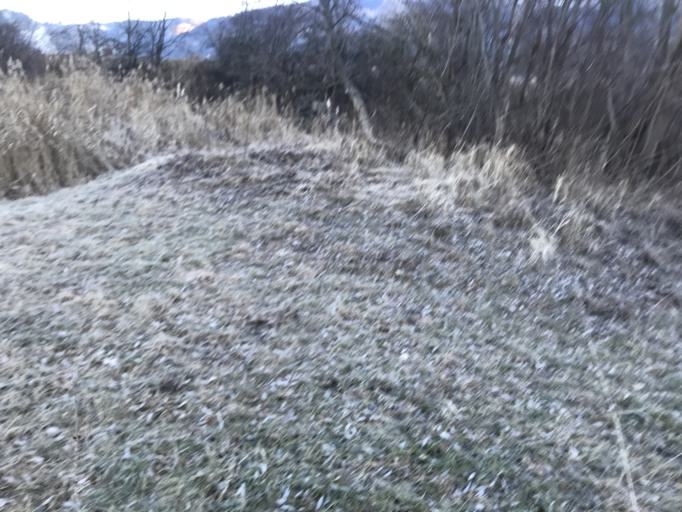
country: IT
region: Trentino-Alto Adige
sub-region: Bolzano
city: Bressanone
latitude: 46.6996
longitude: 11.6527
